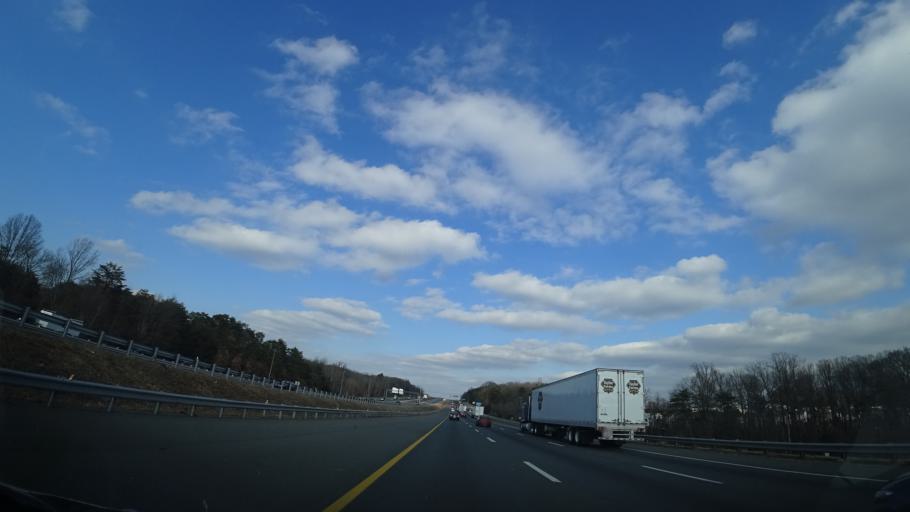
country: US
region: Virginia
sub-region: Prince William County
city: Triangle
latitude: 38.5497
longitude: -77.3432
